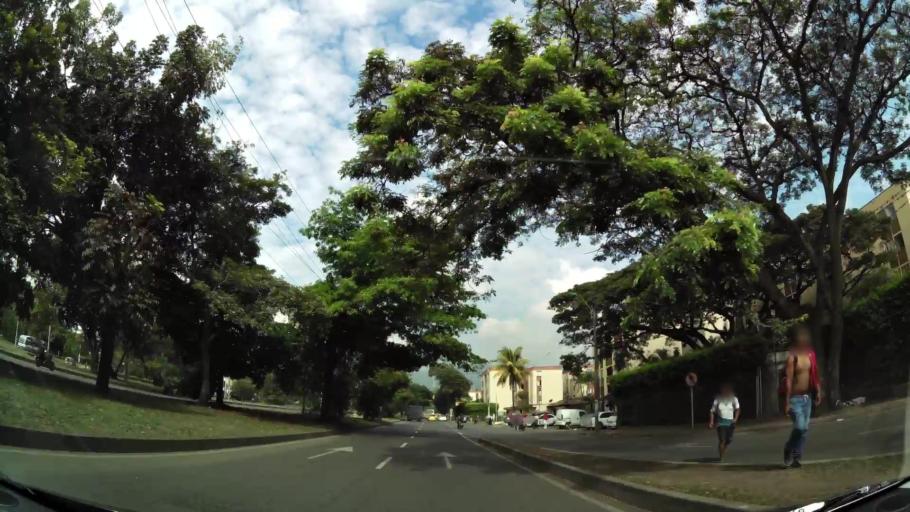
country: CO
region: Valle del Cauca
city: Cali
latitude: 3.4866
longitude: -76.4961
